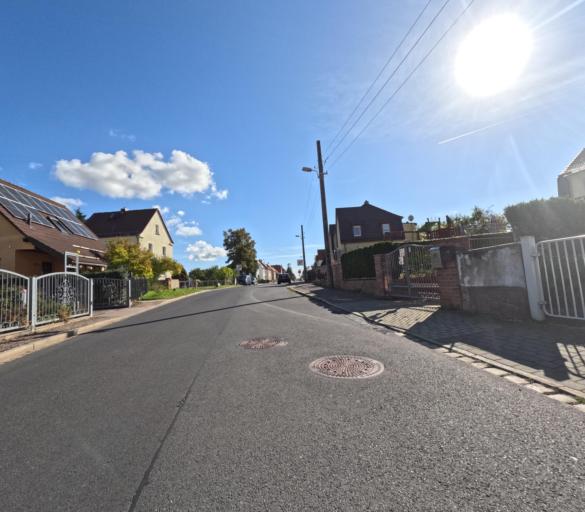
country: DE
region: Saxony
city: Albertstadt
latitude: 51.1186
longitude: 13.7231
